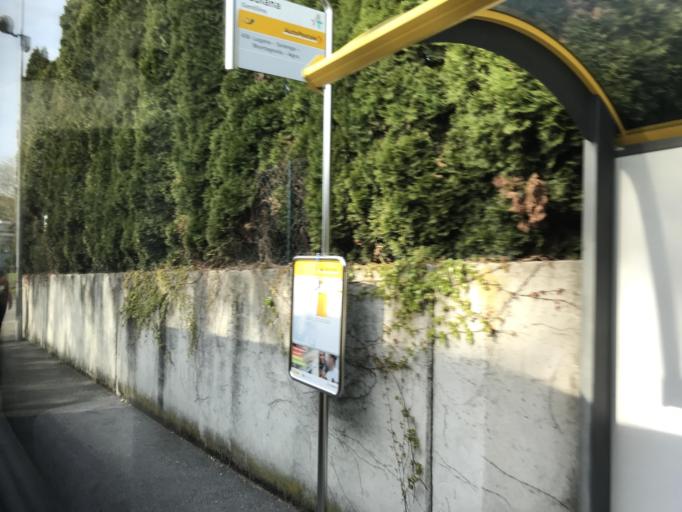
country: CH
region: Ticino
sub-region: Lugano District
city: Sorengo
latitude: 45.9939
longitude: 8.9342
